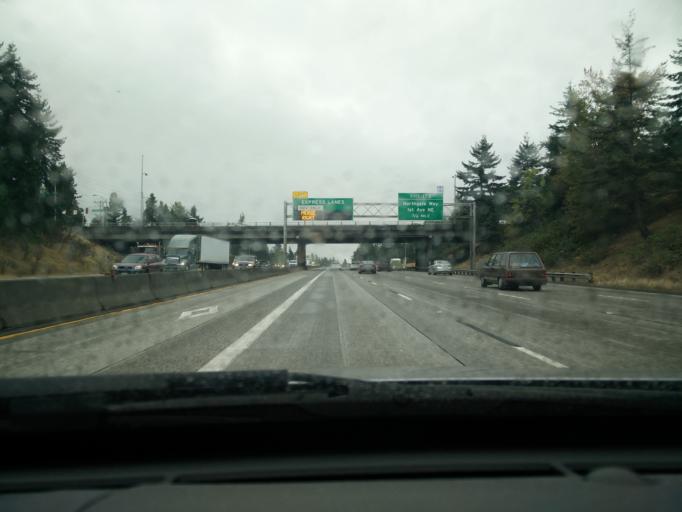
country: US
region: Washington
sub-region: King County
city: Shoreline
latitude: 47.7242
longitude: -122.3244
